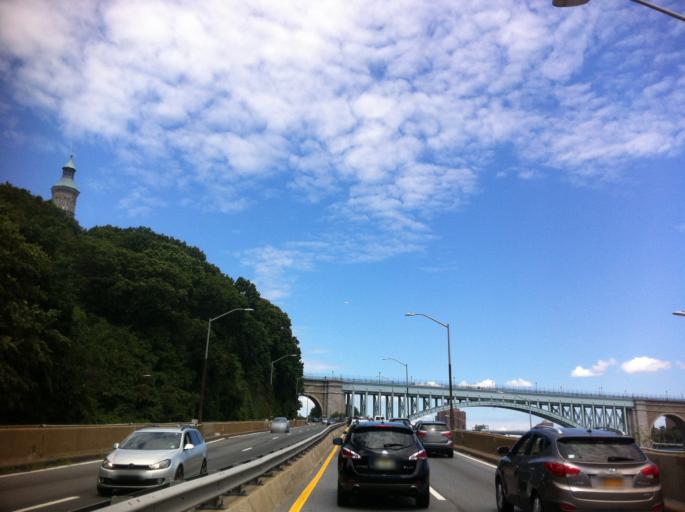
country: US
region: New York
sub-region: New York County
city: Inwood
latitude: 40.8401
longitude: -73.9326
